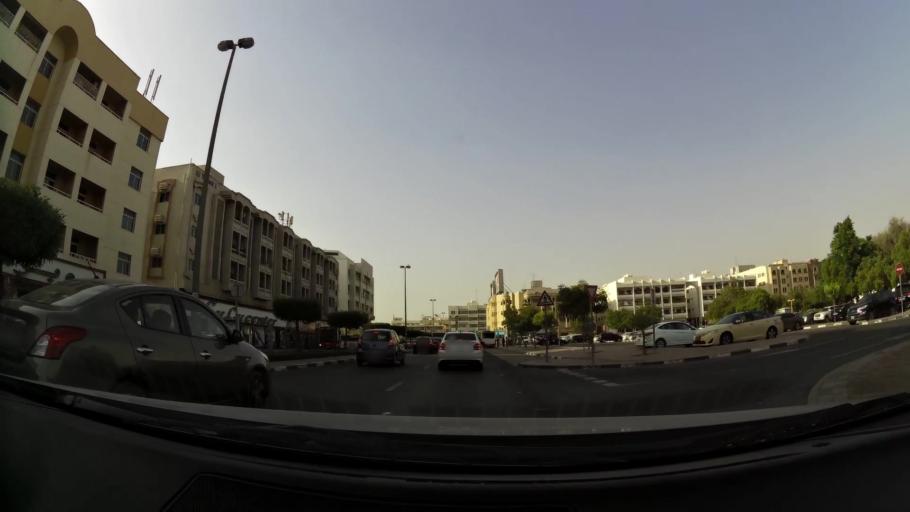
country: AE
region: Ash Shariqah
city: Sharjah
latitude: 25.2432
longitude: 55.3044
